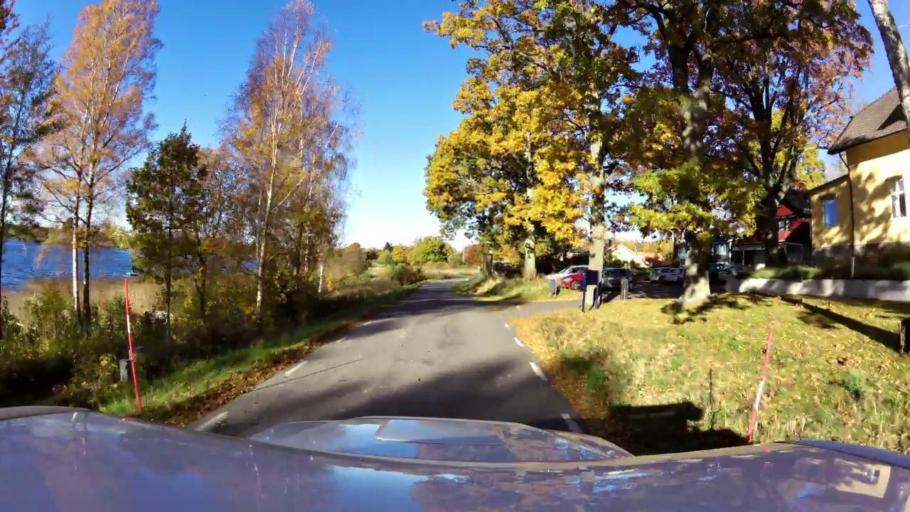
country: SE
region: OEstergoetland
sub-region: Linkopings Kommun
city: Ljungsbro
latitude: 58.5286
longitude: 15.4593
